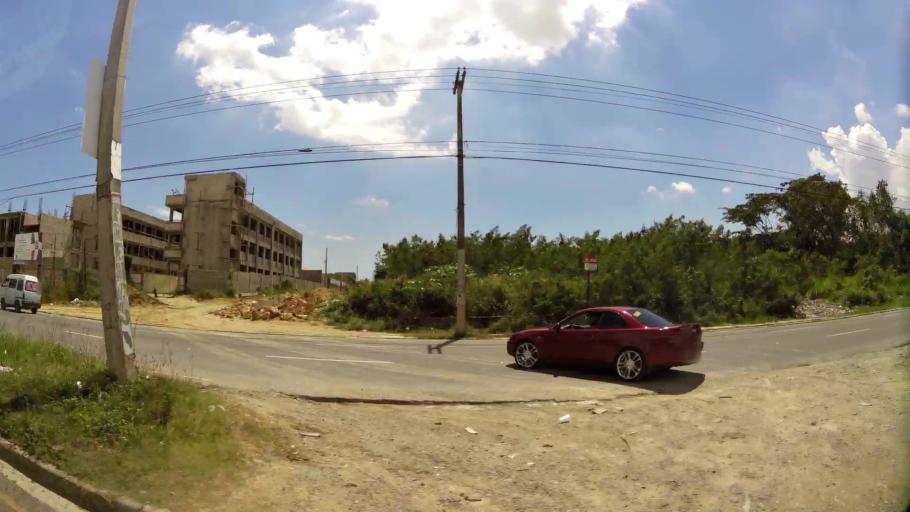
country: DO
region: Nacional
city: Ensanche Luperon
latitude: 18.5450
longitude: -69.8740
